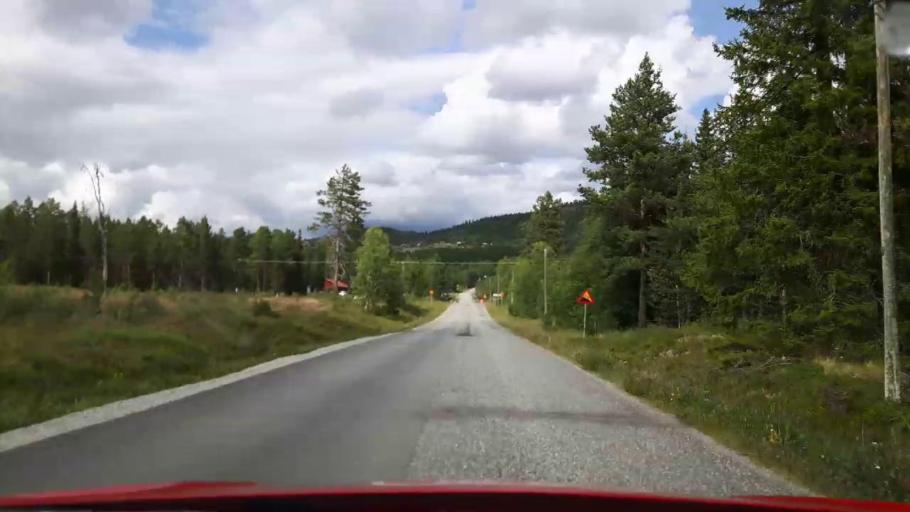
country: NO
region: Hedmark
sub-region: Engerdal
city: Engerdal
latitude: 62.4322
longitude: 12.6796
